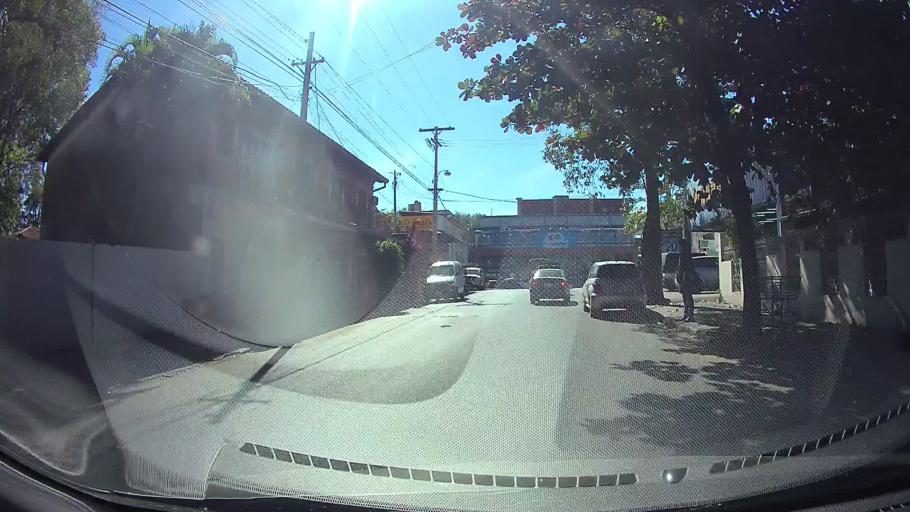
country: PY
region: Central
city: Lambare
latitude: -25.3179
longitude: -57.5724
